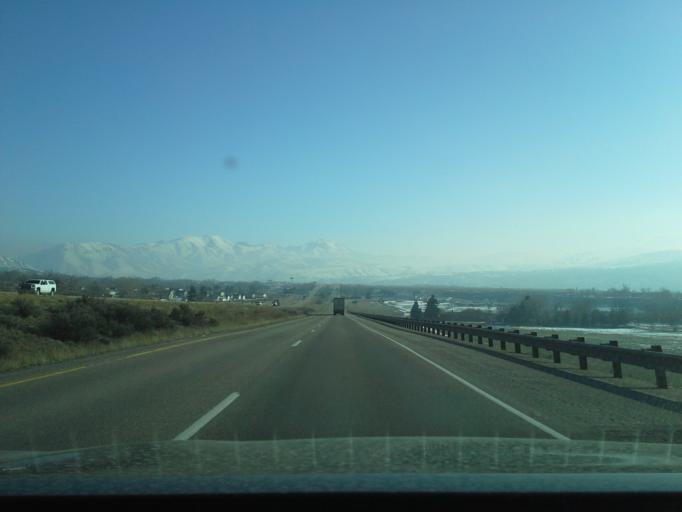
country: US
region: Idaho
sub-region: Bannock County
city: Pocatello
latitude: 42.8489
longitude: -112.4145
